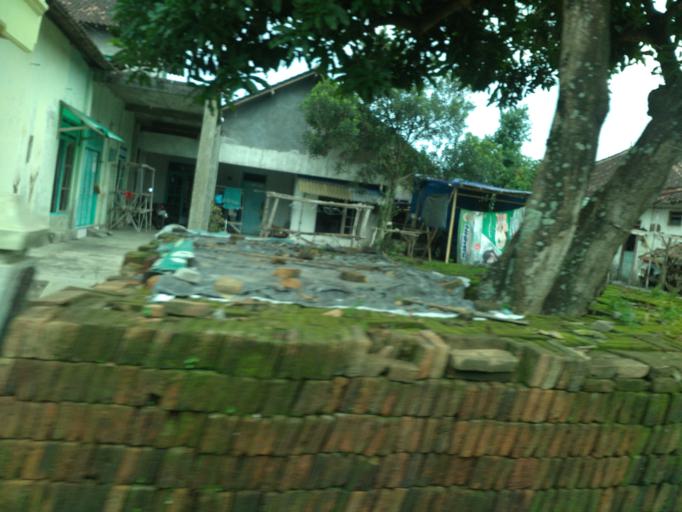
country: ID
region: Central Java
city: Klaten
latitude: -7.6862
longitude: 110.6317
